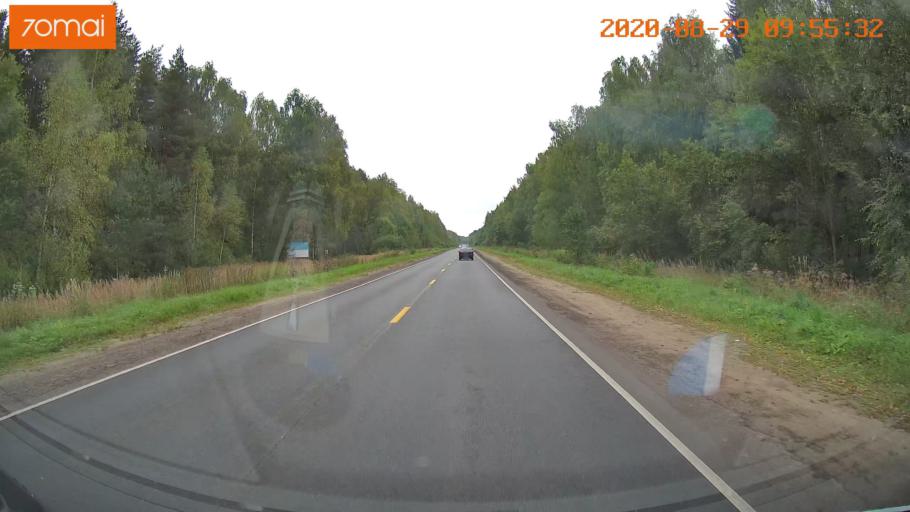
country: RU
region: Ivanovo
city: Zarechnyy
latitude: 57.4221
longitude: 42.2657
